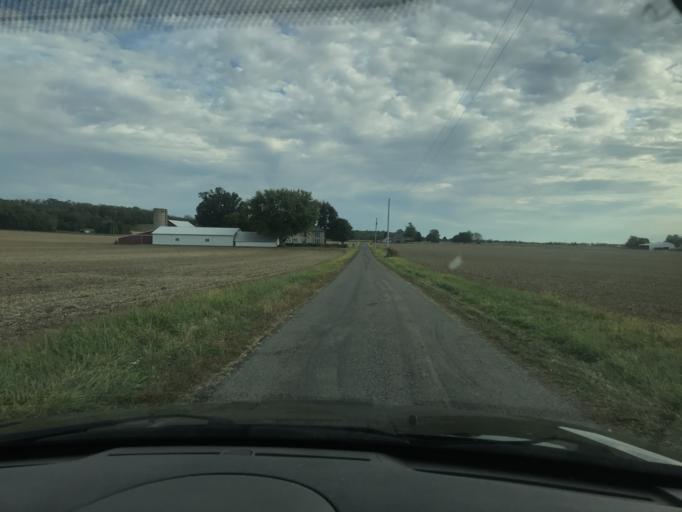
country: US
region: Ohio
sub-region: Logan County
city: West Liberty
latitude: 40.2392
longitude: -83.6865
